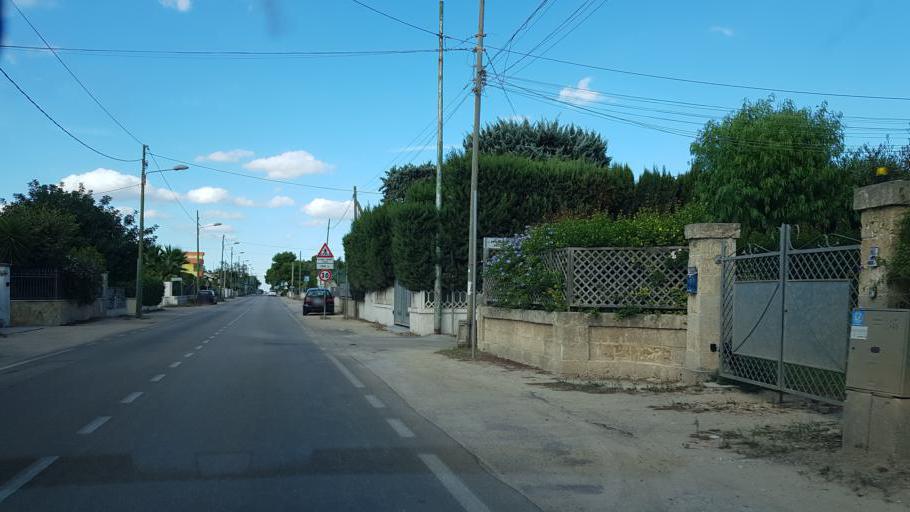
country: IT
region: Apulia
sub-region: Provincia di Lecce
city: Nardo
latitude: 40.1518
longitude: 18.0182
